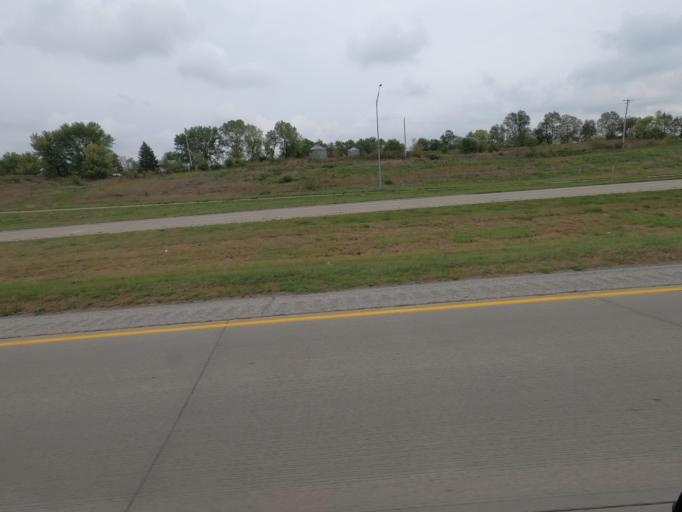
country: US
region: Iowa
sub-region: Wapello County
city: Eddyville
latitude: 41.1453
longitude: -92.6184
